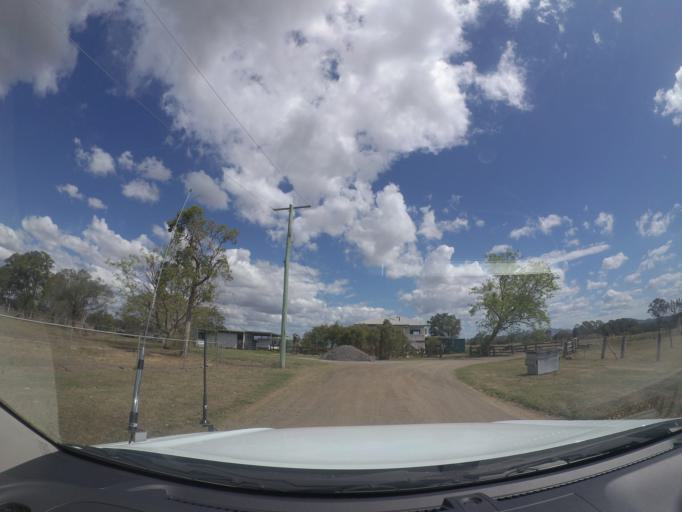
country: AU
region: Queensland
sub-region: Logan
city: Cedar Vale
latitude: -27.8975
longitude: 152.9583
